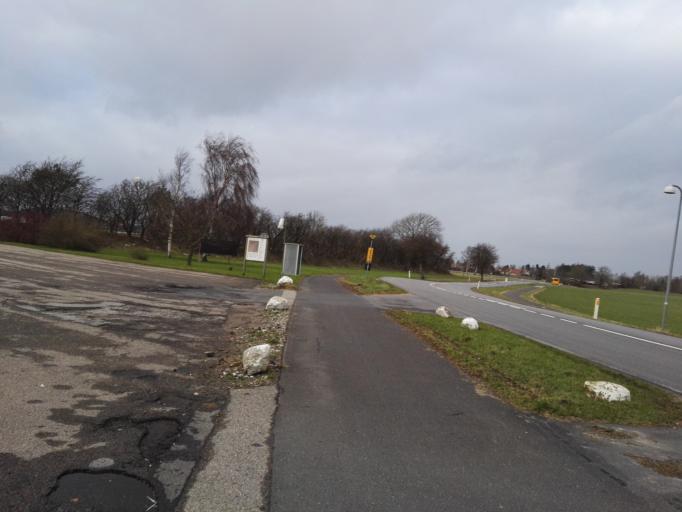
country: DK
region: Zealand
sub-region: Lejre Kommune
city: Ejby
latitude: 55.6983
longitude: 11.9063
